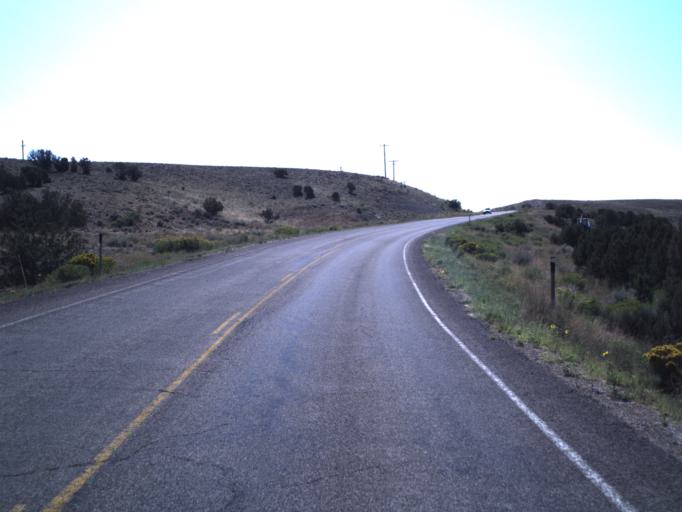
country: US
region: Utah
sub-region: Duchesne County
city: Duchesne
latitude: 40.2524
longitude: -110.3997
